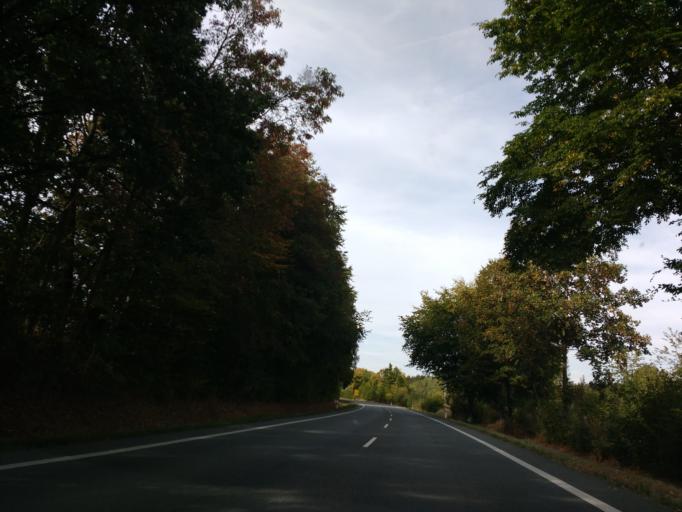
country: DE
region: North Rhine-Westphalia
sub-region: Regierungsbezirk Detmold
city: Willebadessen
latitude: 51.6244
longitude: 9.1392
